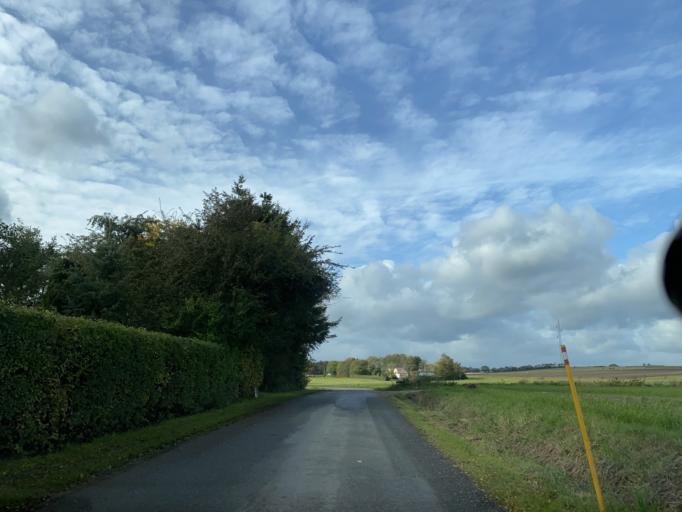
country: DK
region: Central Jutland
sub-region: Arhus Kommune
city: Sabro
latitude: 56.1949
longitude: 9.9998
